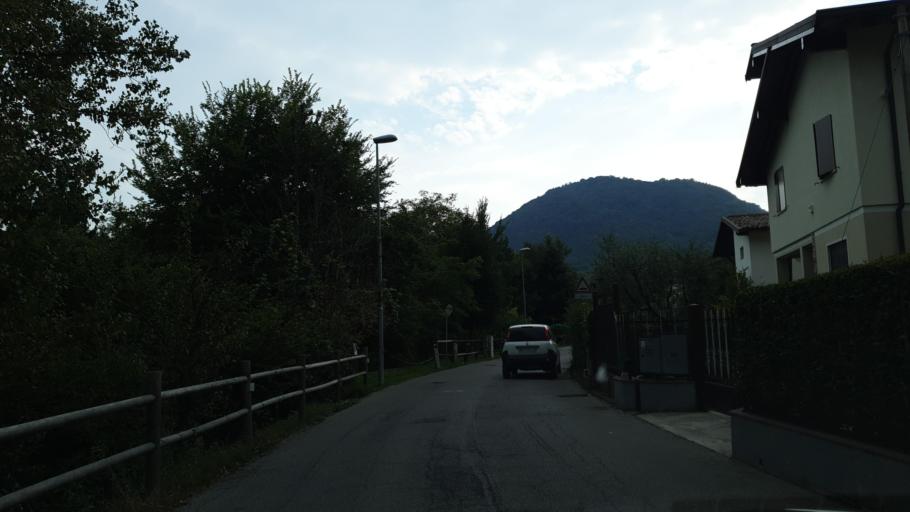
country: IT
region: Lombardy
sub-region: Provincia di Brescia
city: Roe Volciano
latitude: 45.6127
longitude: 10.4807
